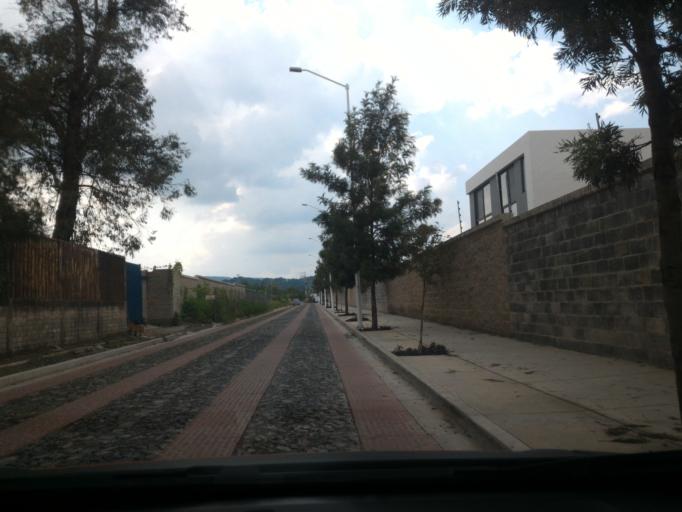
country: MX
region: Jalisco
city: Nuevo Mexico
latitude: 20.6987
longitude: -103.4669
